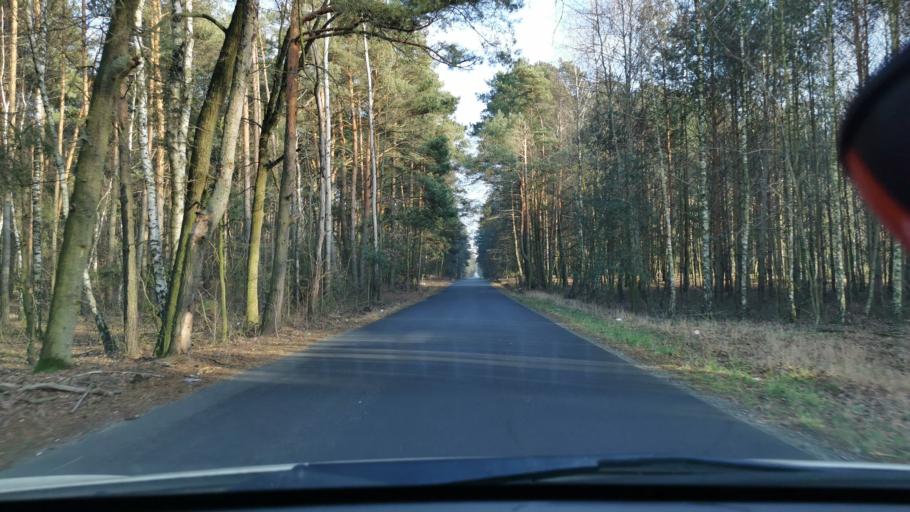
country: PL
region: Greater Poland Voivodeship
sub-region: Powiat kaliski
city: Opatowek
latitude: 51.6601
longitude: 18.2627
